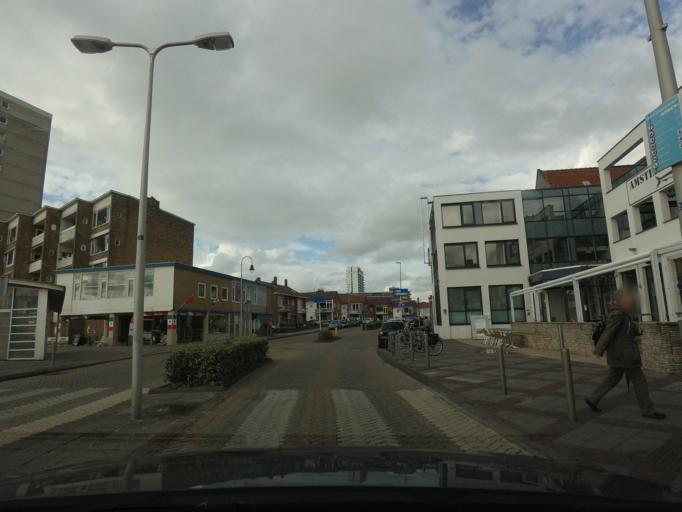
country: NL
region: North Holland
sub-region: Gemeente Zandvoort
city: Zandvoort
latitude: 52.3725
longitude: 4.5263
